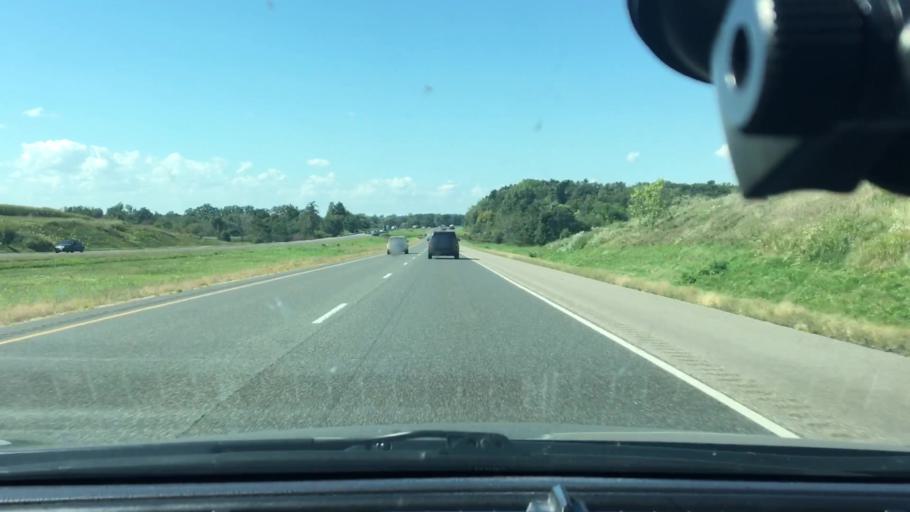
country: US
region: Wisconsin
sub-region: Saint Croix County
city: Woodville
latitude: 44.9345
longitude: -92.2443
